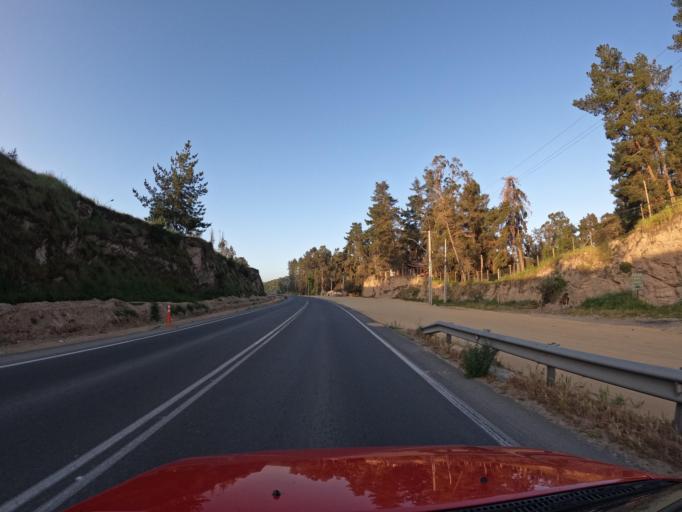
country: CL
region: O'Higgins
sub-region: Provincia de Cachapoal
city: San Vicente
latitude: -34.1451
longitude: -71.3798
